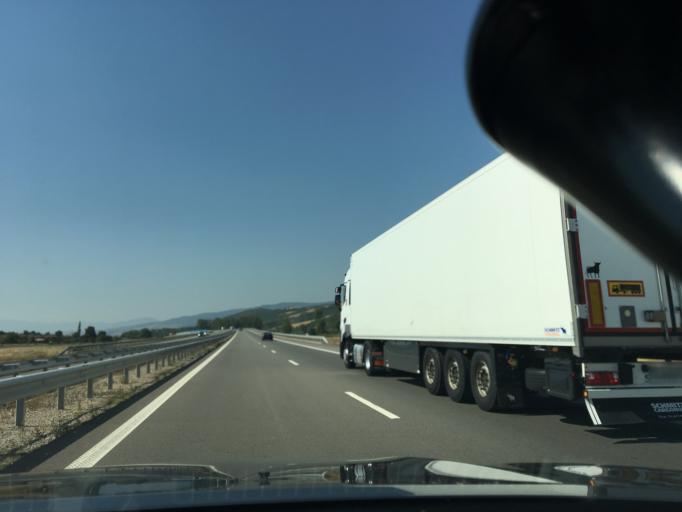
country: BG
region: Kyustendil
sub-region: Obshtina Boboshevo
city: Boboshevo
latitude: 42.1997
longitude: 23.0545
